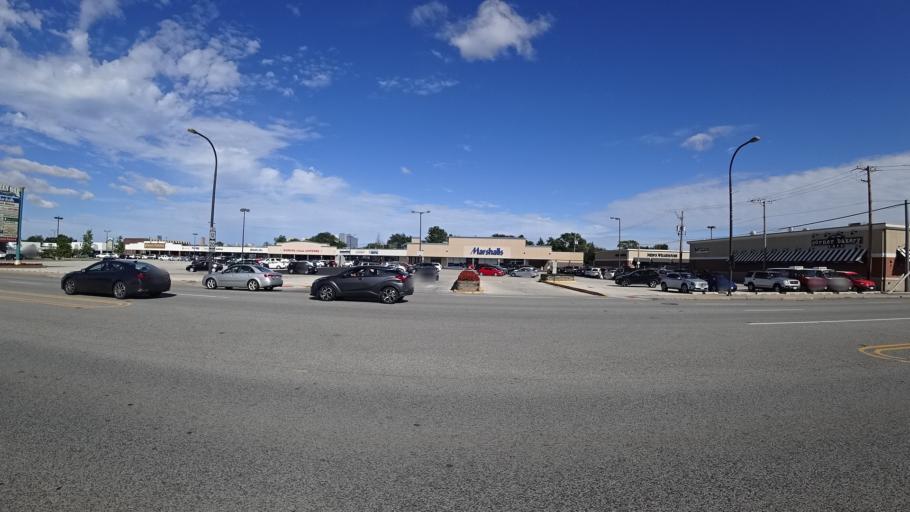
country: US
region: Illinois
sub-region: Cook County
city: Hometown
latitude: 41.7184
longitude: -87.7408
